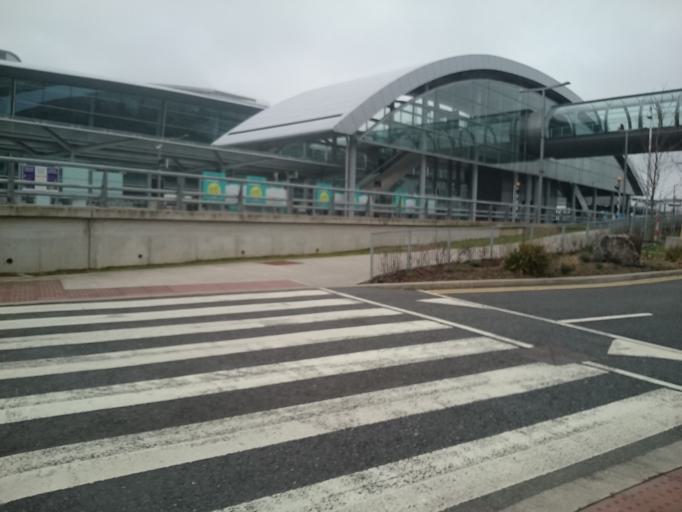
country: IE
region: Leinster
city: Beaumont
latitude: 53.4267
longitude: -6.2385
